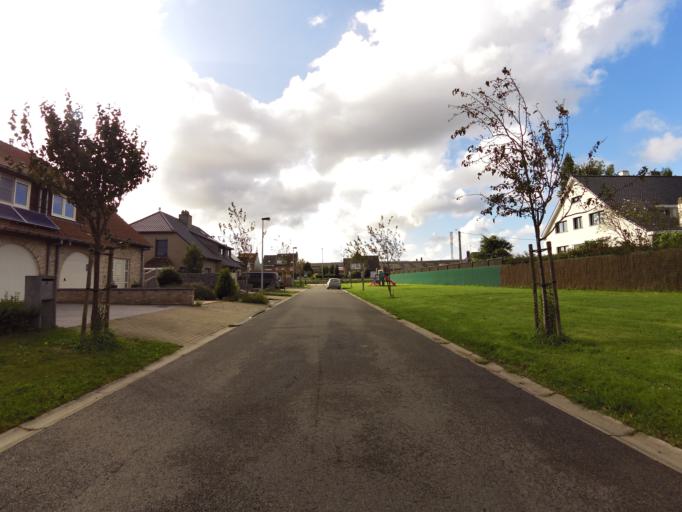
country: BE
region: Flanders
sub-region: Provincie West-Vlaanderen
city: Middelkerke
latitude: 51.1723
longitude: 2.8771
